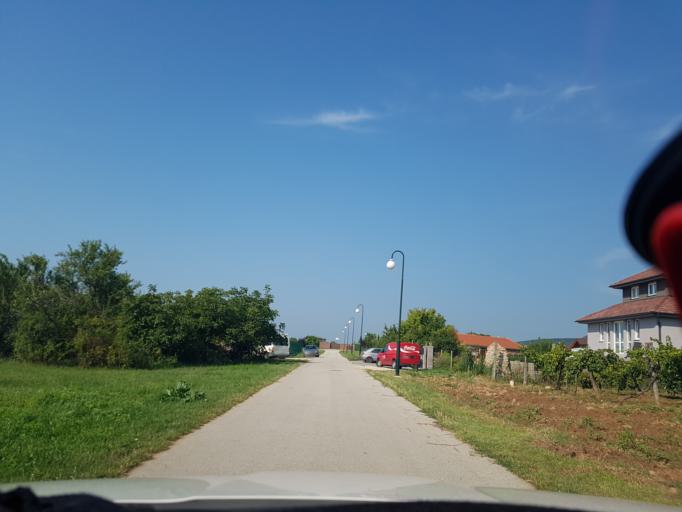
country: HU
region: Veszprem
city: Csopak
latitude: 46.9910
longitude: 17.9679
